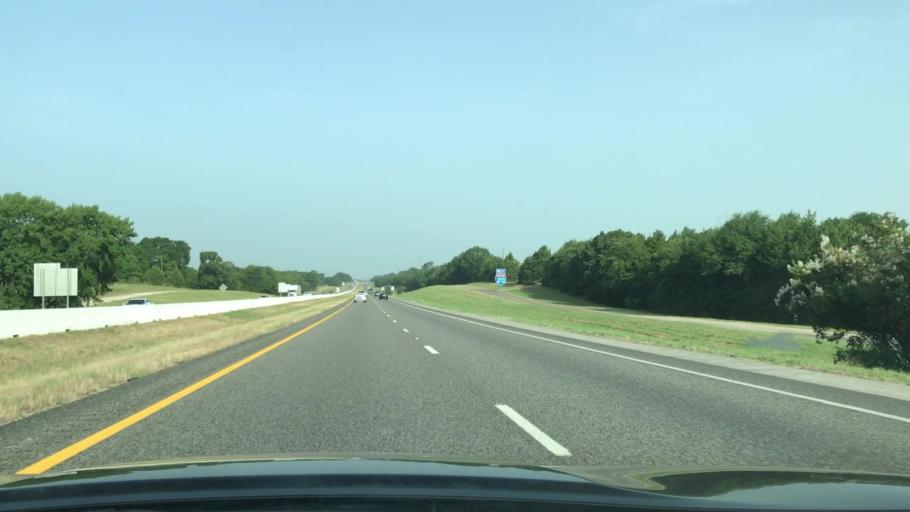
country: US
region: Texas
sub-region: Van Zandt County
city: Van
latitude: 32.5080
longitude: -95.6502
